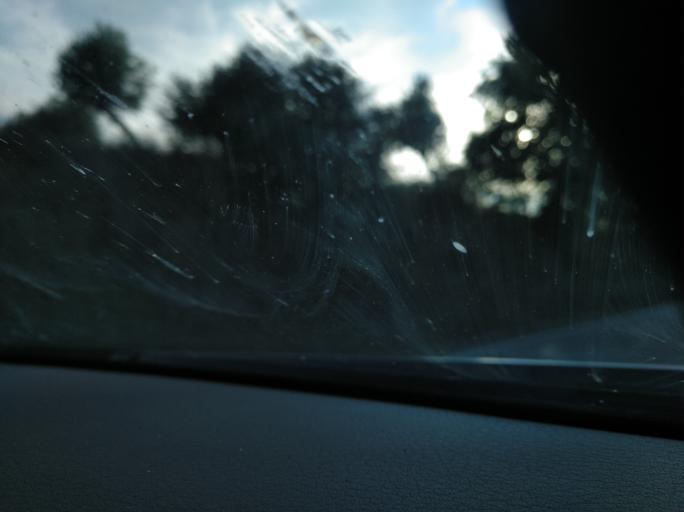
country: PT
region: Evora
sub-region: Estremoz
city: Estremoz
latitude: 38.9611
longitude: -7.5773
